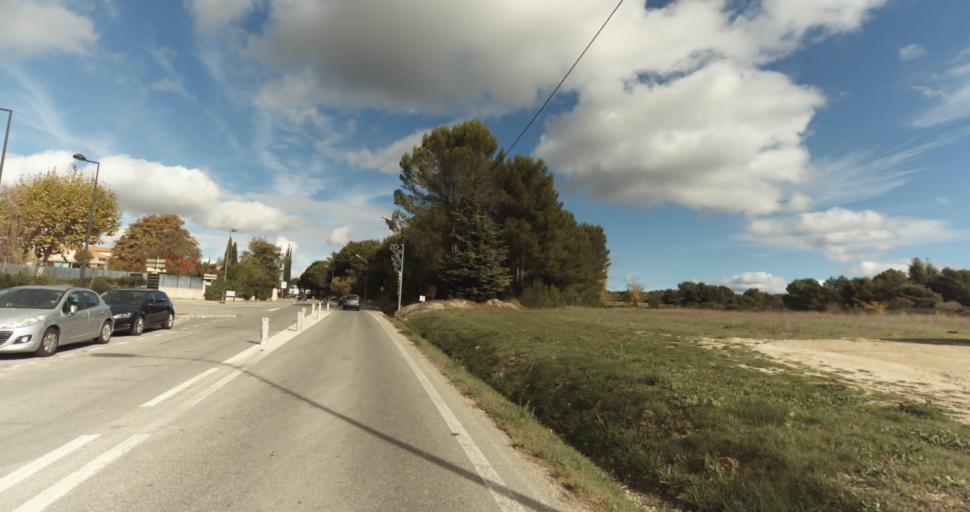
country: FR
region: Provence-Alpes-Cote d'Azur
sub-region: Departement des Bouches-du-Rhone
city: Venelles
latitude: 43.5923
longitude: 5.4810
